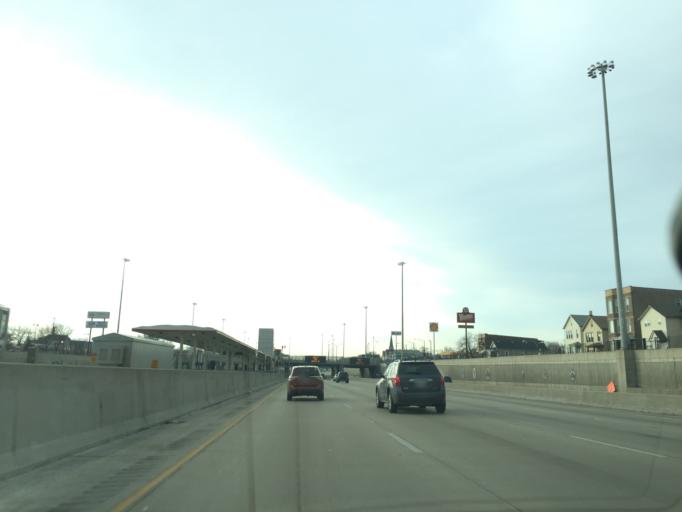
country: US
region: Illinois
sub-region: Cook County
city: Chicago
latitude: 41.7969
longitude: -87.6314
